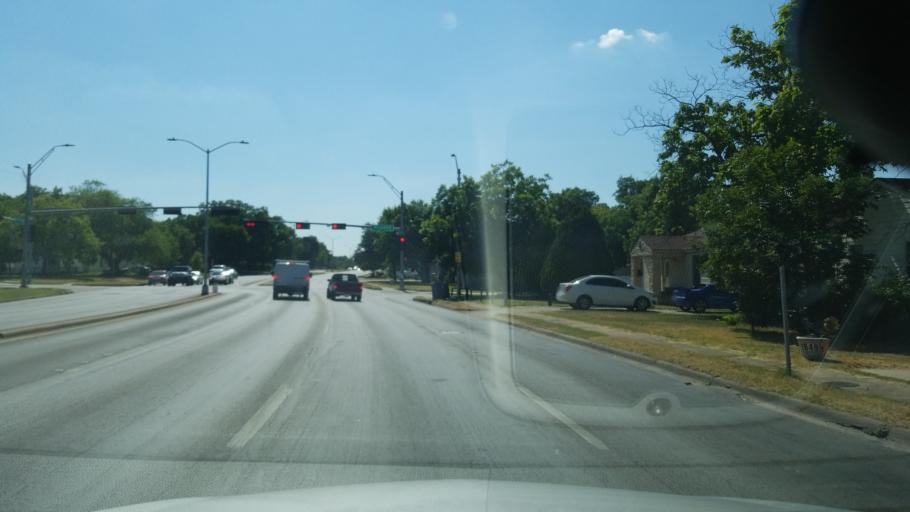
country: US
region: Texas
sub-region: Dallas County
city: Cockrell Hill
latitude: 32.7205
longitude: -96.8480
